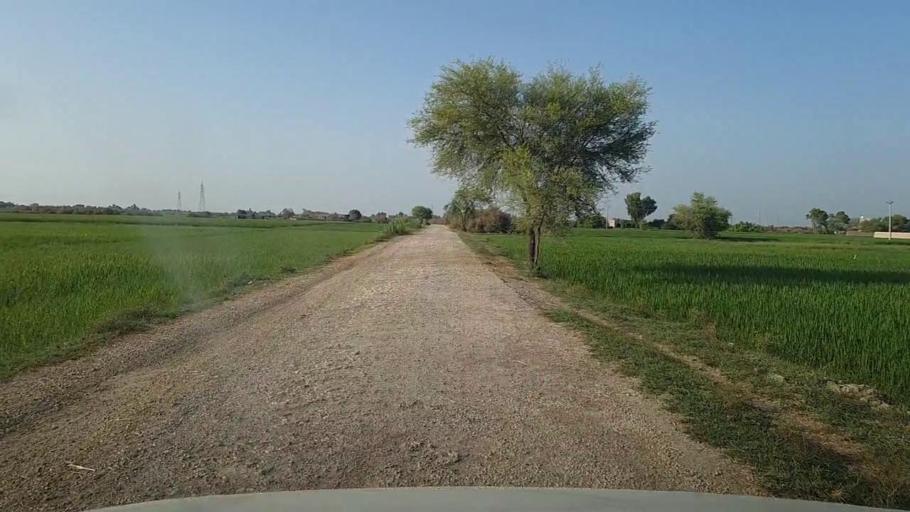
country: PK
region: Sindh
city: Kandhkot
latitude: 28.3019
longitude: 69.3287
